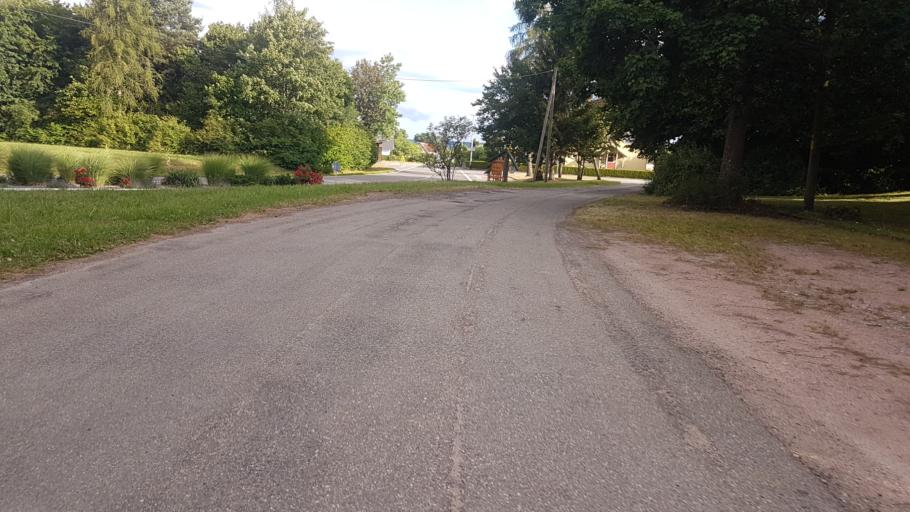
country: DE
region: Baden-Wuerttemberg
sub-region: Freiburg Region
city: Unterkirnach
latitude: 48.0066
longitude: 8.4097
